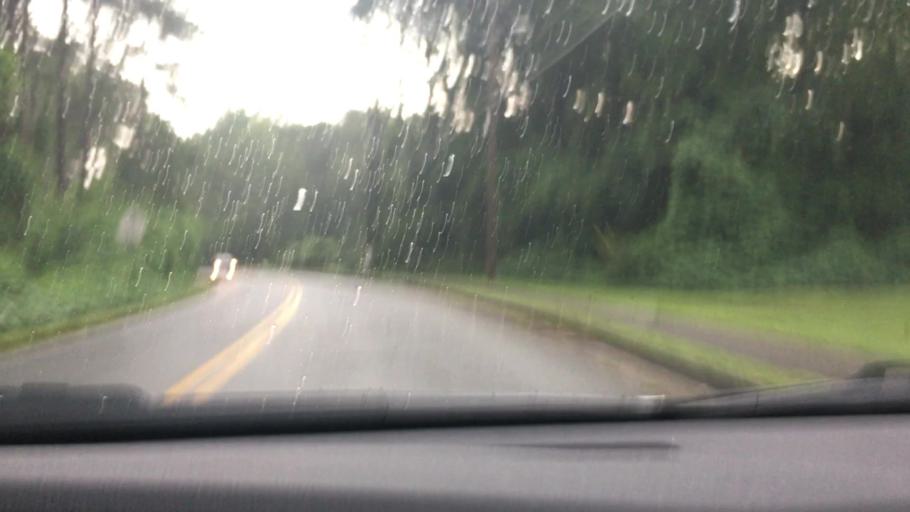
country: US
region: Georgia
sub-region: Fulton County
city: Union City
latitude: 33.6347
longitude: -84.5309
